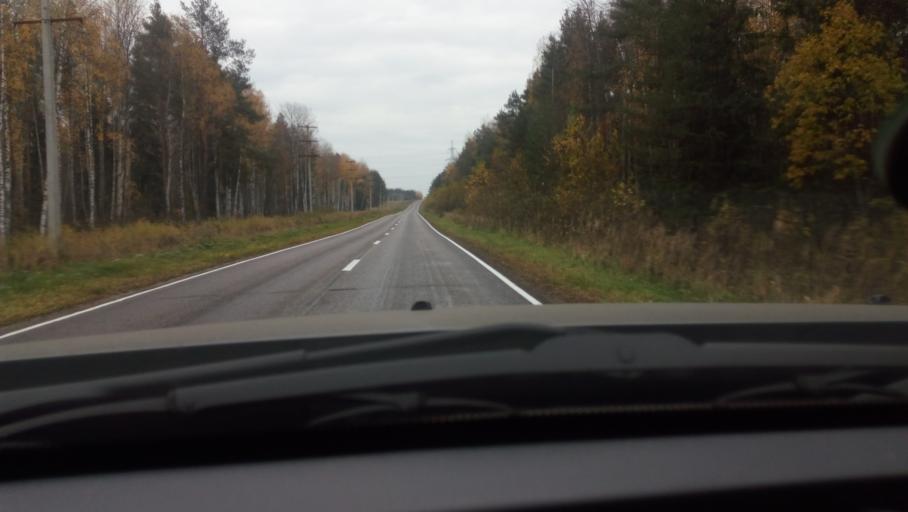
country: RU
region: Moskovskaya
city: Avsyunino
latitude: 55.5991
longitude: 39.2197
